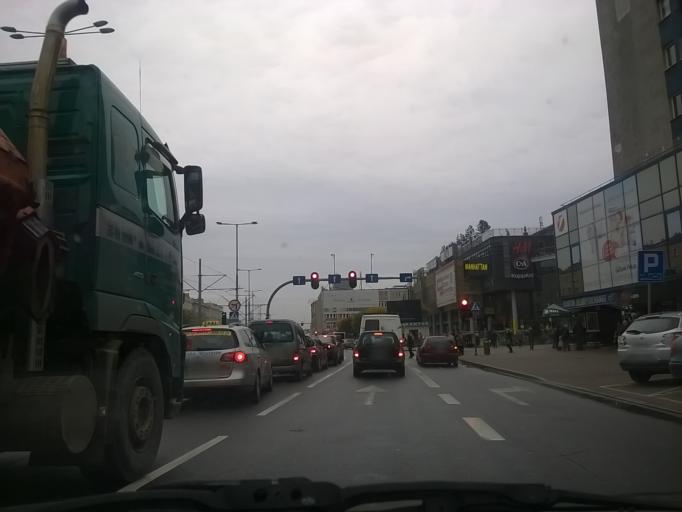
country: PL
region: Pomeranian Voivodeship
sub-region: Gdansk
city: Gdansk
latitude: 54.3783
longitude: 18.6063
